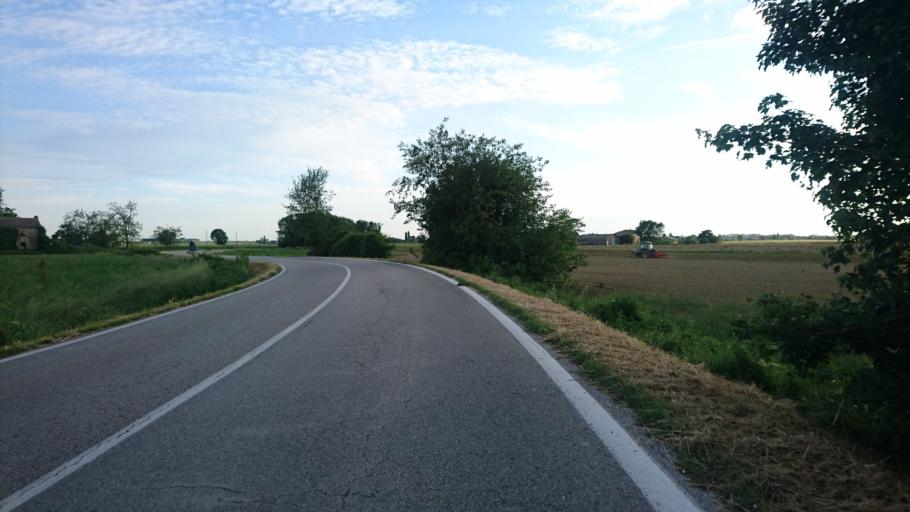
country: IT
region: Veneto
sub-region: Provincia di Rovigo
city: Ceneselli
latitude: 45.0215
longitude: 11.3467
